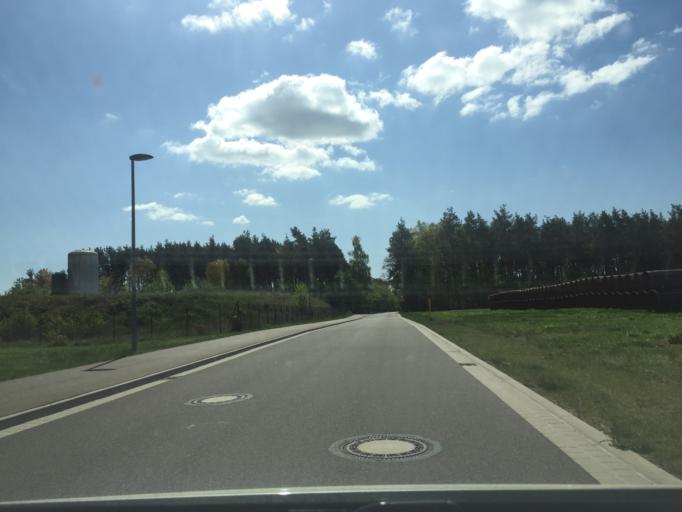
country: DE
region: Mecklenburg-Vorpommern
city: Torgelow
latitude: 53.6360
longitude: 13.9938
